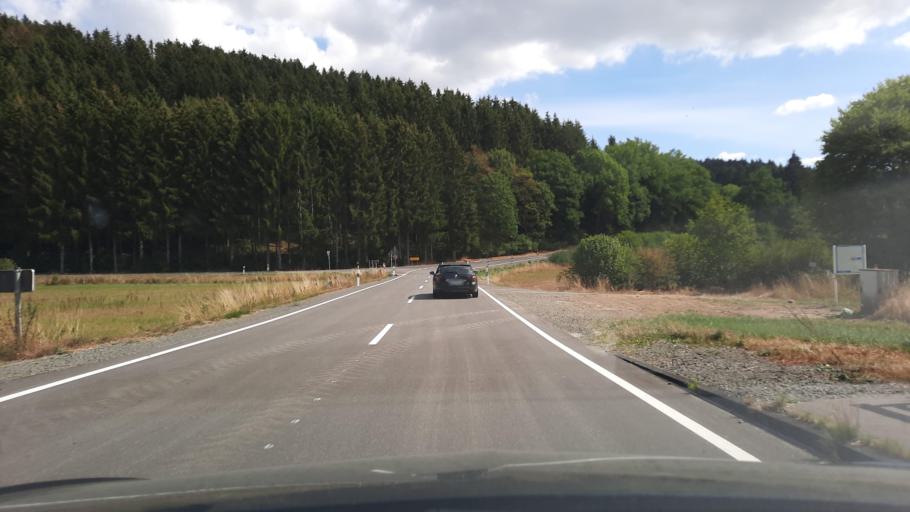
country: DE
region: Rheinland-Pfalz
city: Prum
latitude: 50.2166
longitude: 6.3920
